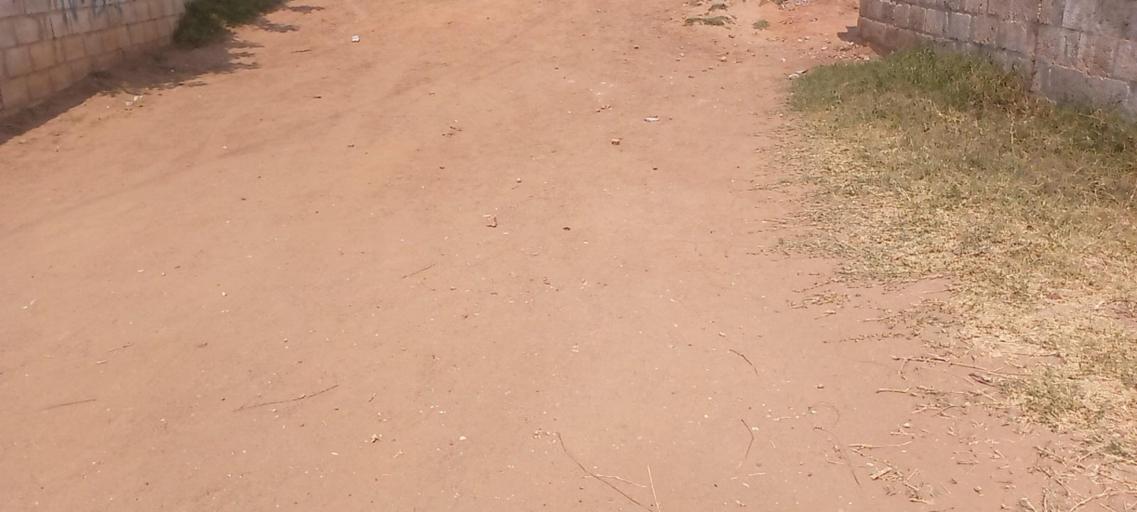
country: ZM
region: Lusaka
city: Lusaka
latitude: -15.4088
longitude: 28.3590
